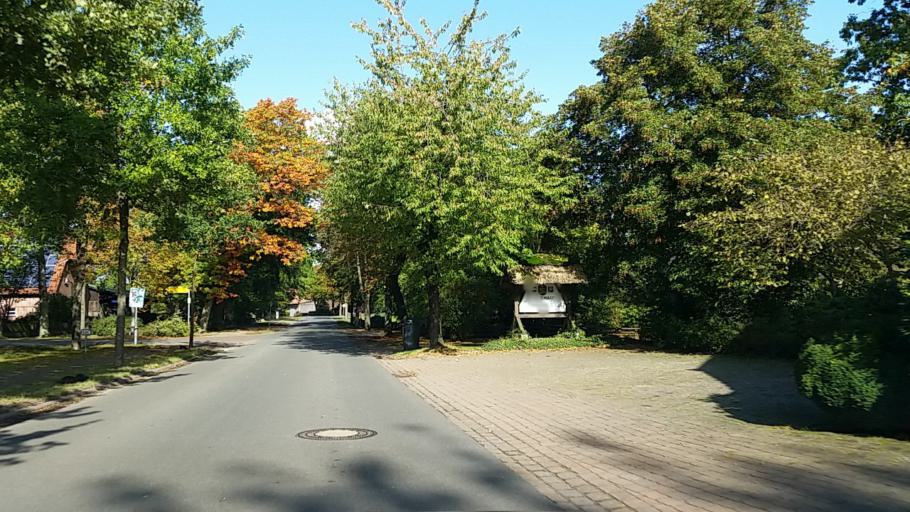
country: DE
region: Lower Saxony
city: Neuenkirchen
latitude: 53.0560
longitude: 9.7396
